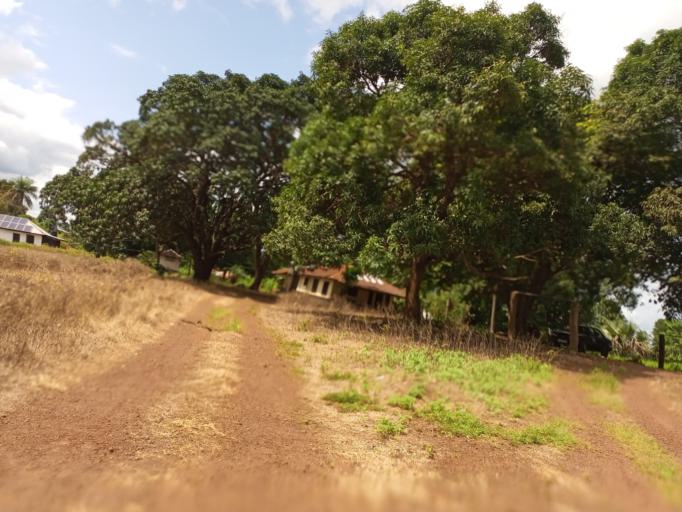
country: SL
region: Northern Province
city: Kamakwie
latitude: 9.4984
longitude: -12.2357
